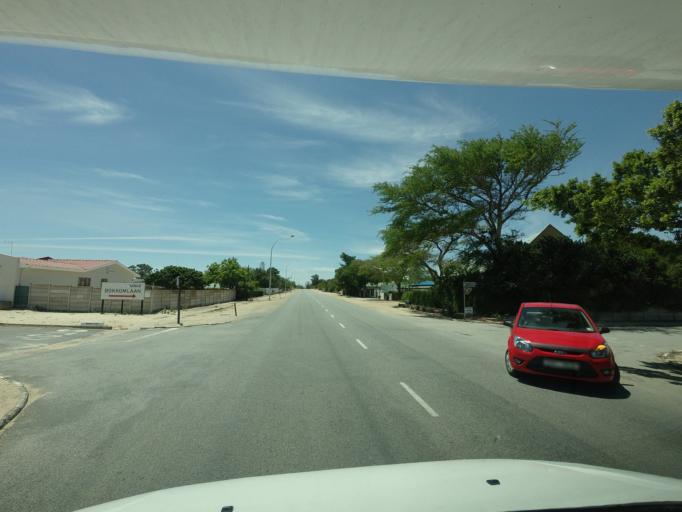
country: ZA
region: Western Cape
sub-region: West Coast District Municipality
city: Vredenburg
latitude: -32.7874
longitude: 18.1828
